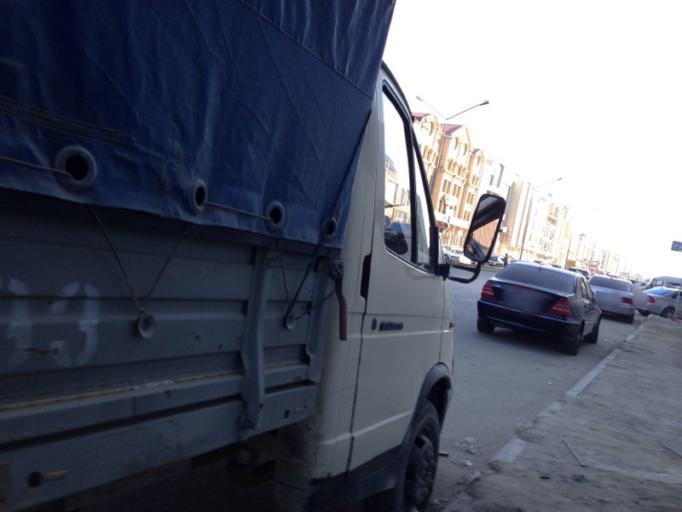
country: AZ
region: Baki
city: Baku
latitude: 40.4147
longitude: 49.8594
